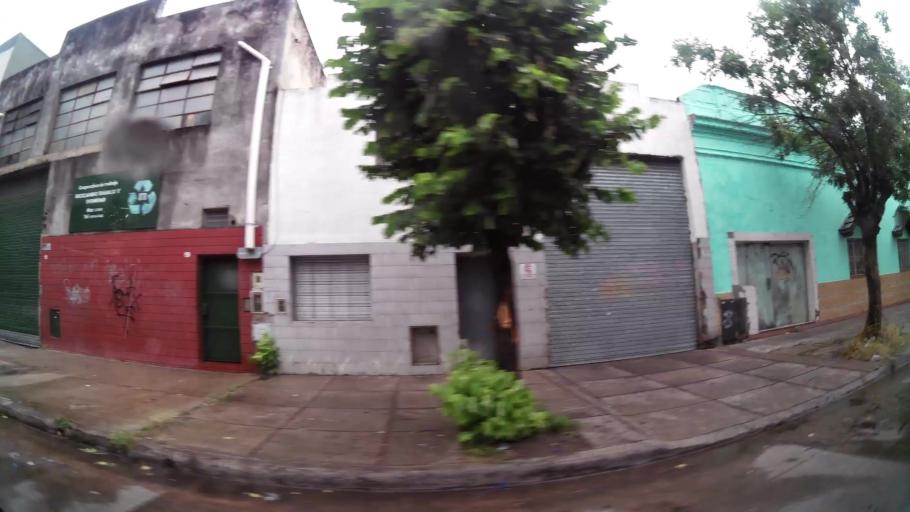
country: AR
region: Buenos Aires F.D.
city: Villa Lugano
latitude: -34.6629
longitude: -58.4402
